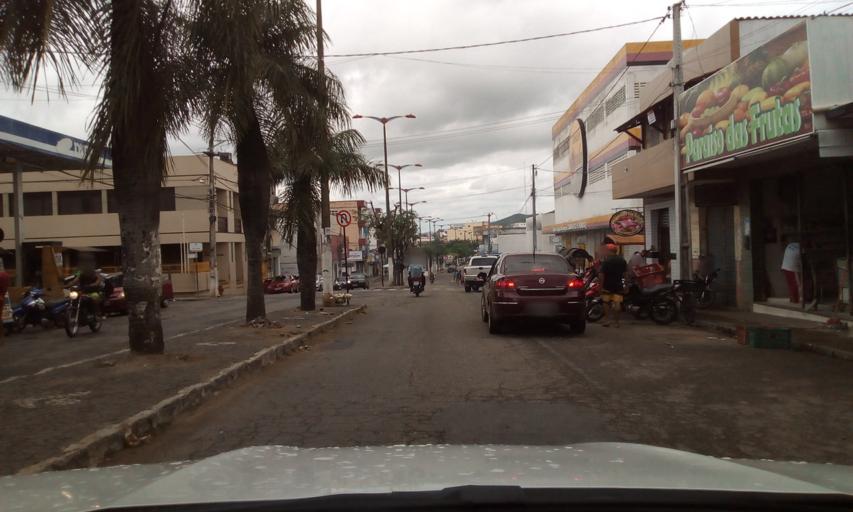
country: BR
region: Paraiba
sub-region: Guarabira
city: Guarabira
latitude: -6.8495
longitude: -35.4905
